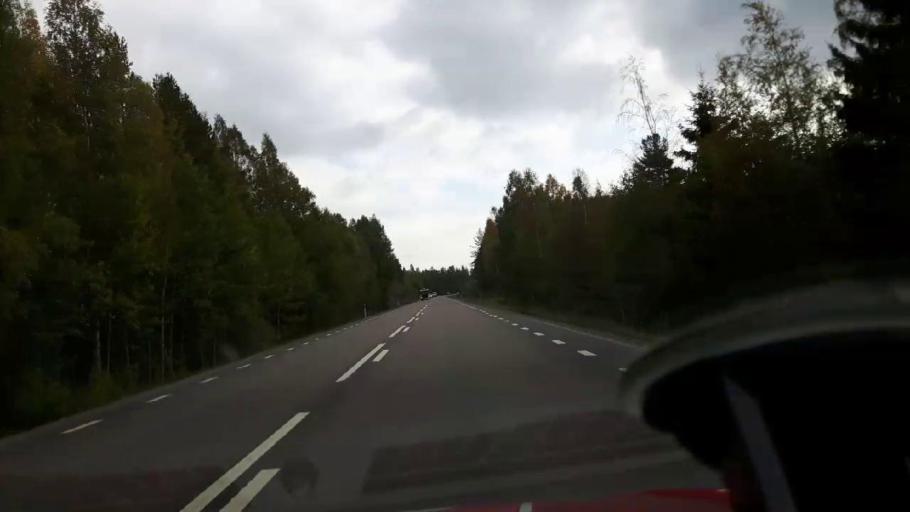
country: SE
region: Gaevleborg
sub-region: Bollnas Kommun
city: Kilafors
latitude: 61.2726
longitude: 16.5320
